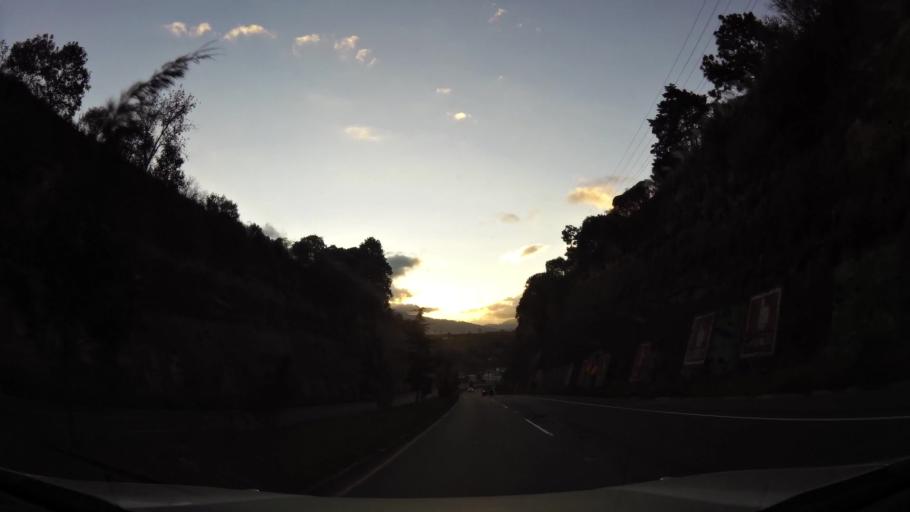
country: GT
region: Totonicapan
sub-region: Municipio de San Andres Xecul
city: San Andres Xecul
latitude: 14.8638
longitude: -91.4851
